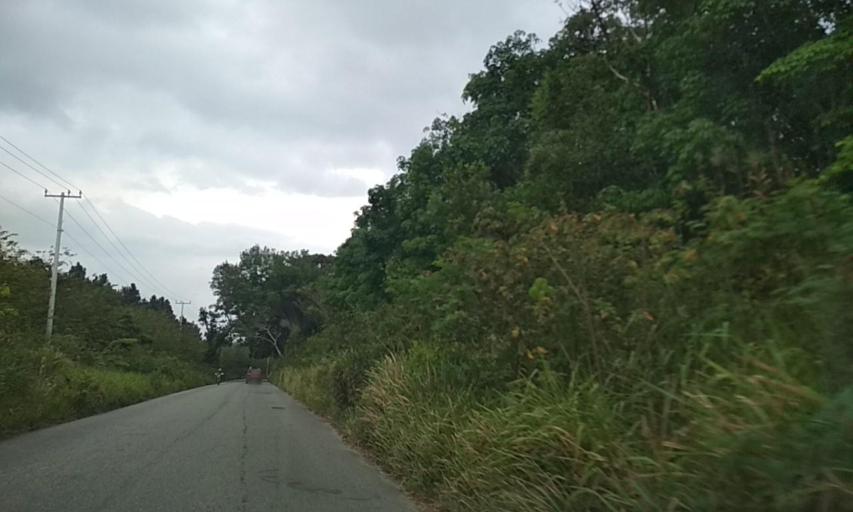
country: MX
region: Veracruz
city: Las Choapas
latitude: 17.8111
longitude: -94.1088
